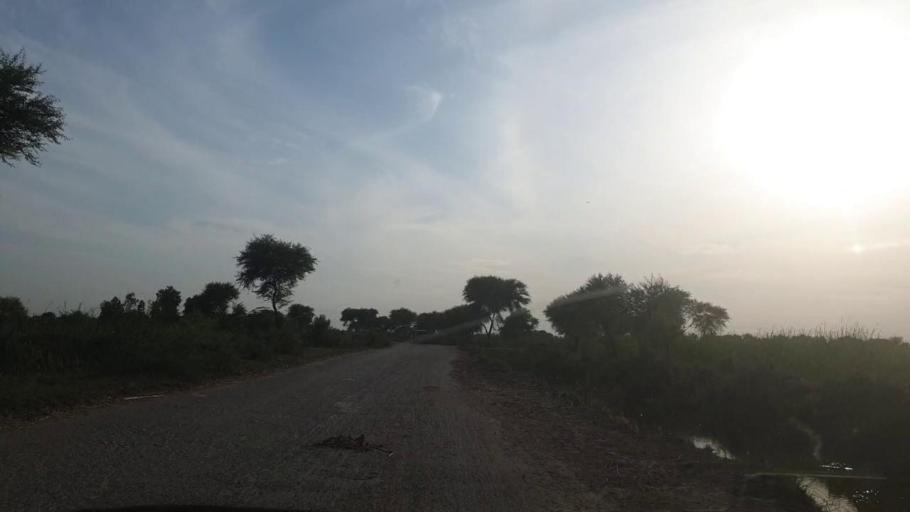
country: PK
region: Sindh
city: Tando Muhammad Khan
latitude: 25.2025
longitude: 68.4981
